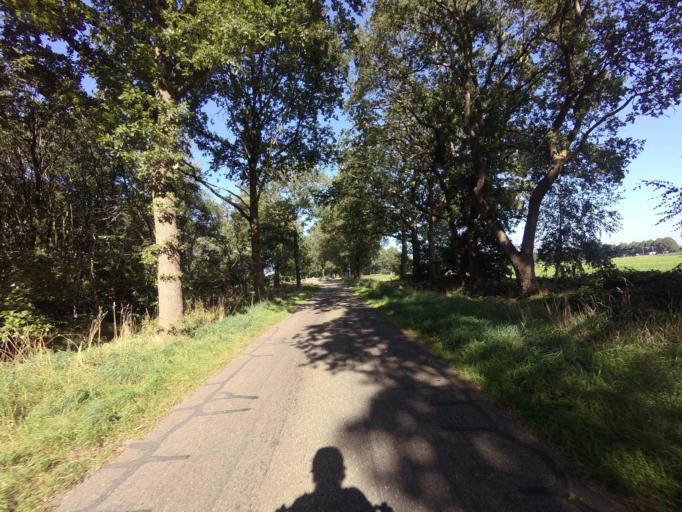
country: NL
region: Overijssel
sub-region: Gemeente Hardenberg
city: Hardenberg
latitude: 52.5257
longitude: 6.6017
